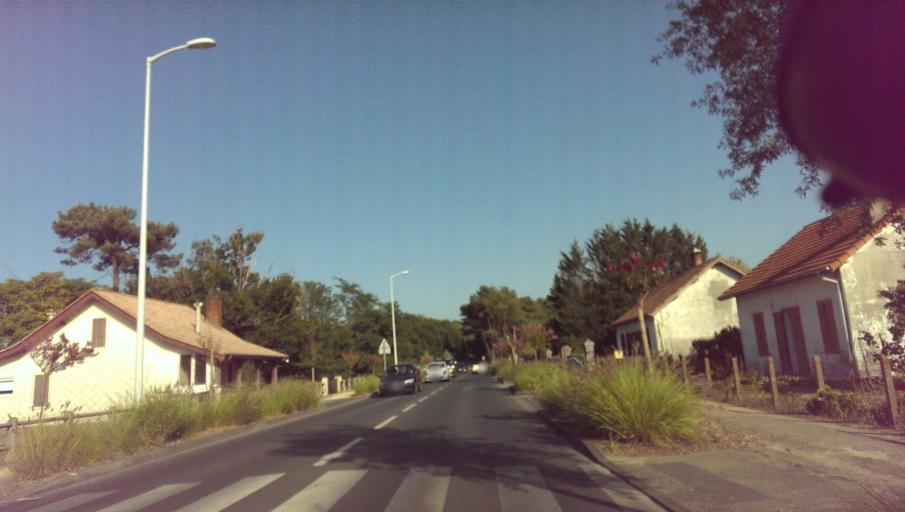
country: FR
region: Aquitaine
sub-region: Departement des Landes
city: Mimizan
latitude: 44.2072
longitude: -1.2418
